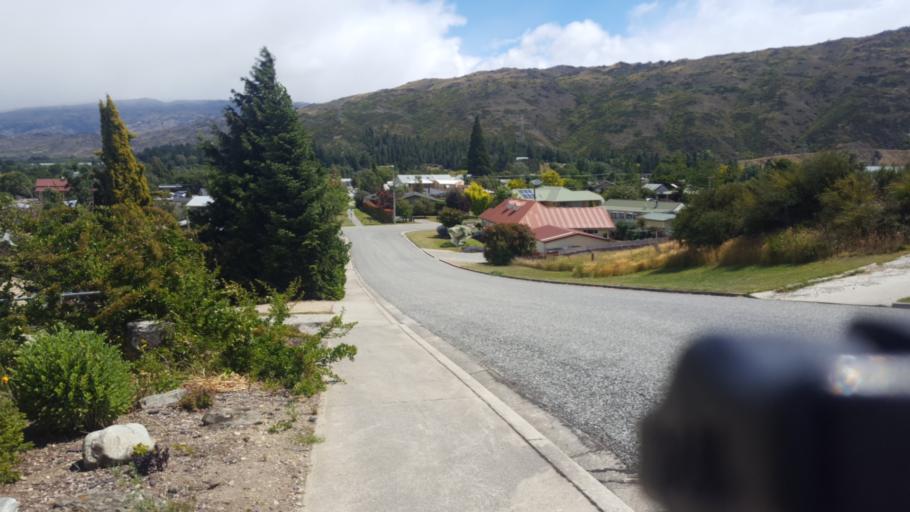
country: NZ
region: Otago
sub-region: Queenstown-Lakes District
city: Wanaka
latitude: -45.1863
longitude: 169.3228
